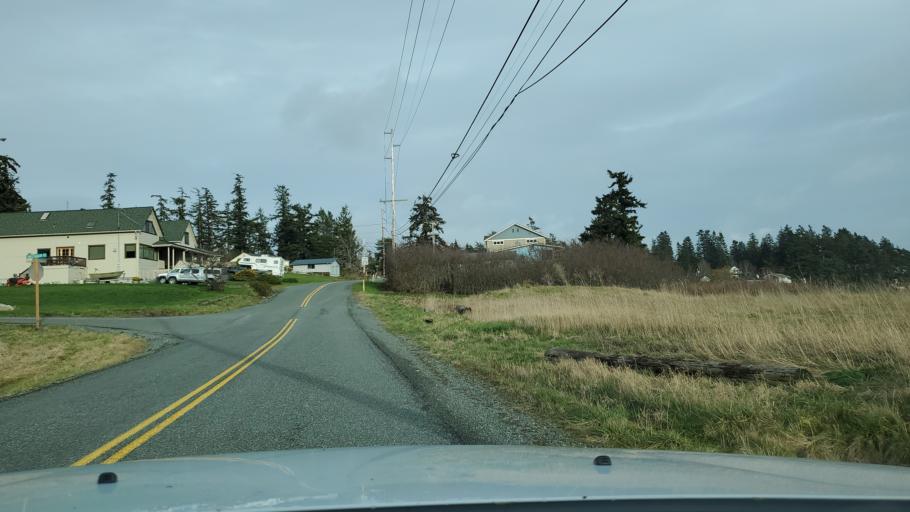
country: US
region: Washington
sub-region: Skagit County
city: Anacortes
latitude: 48.4479
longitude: -122.5737
